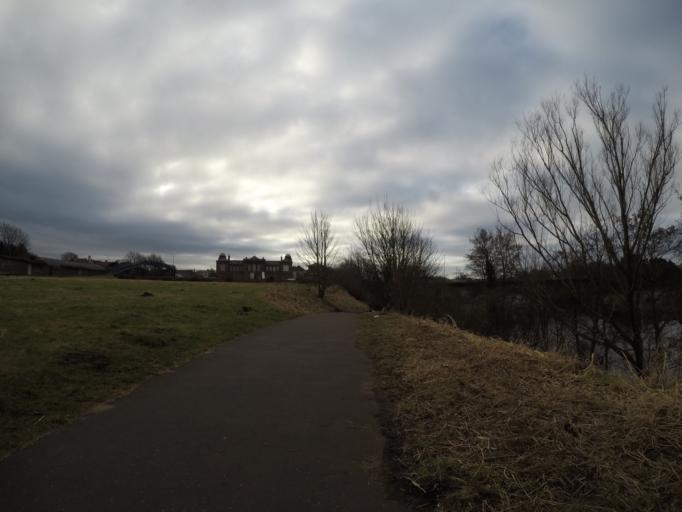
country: GB
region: Scotland
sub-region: North Ayrshire
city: Irvine
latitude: 55.6198
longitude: -4.6730
